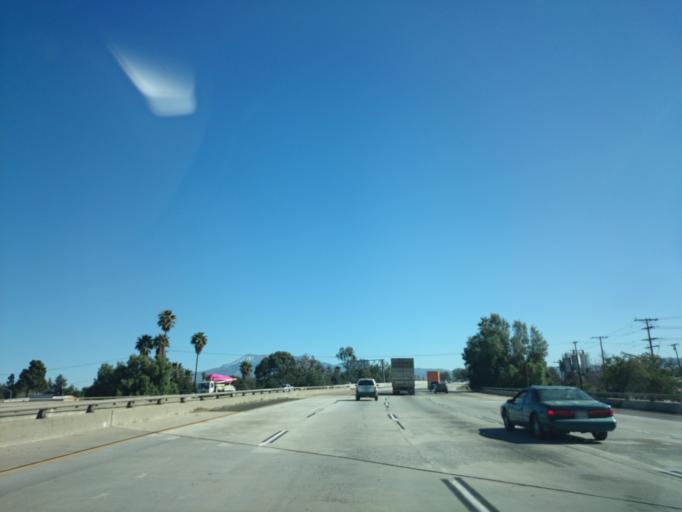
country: US
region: California
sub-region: Riverside County
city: Beaumont
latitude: 33.9315
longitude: -116.9868
